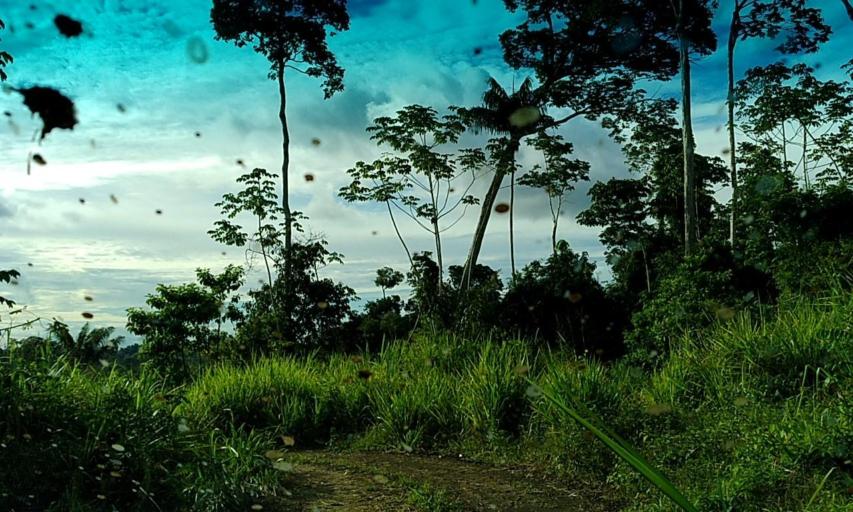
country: BR
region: Para
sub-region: Senador Jose Porfirio
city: Senador Jose Porfirio
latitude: -3.0060
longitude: -51.7496
